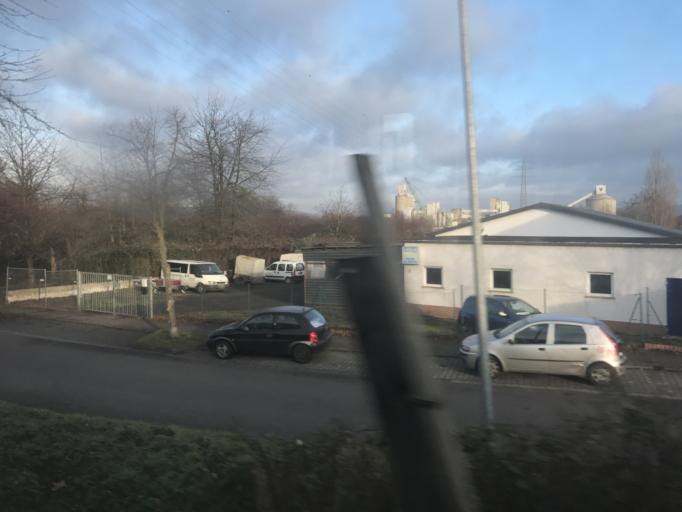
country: DE
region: Rheinland-Pfalz
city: Kettig
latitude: 50.4101
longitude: 7.4719
